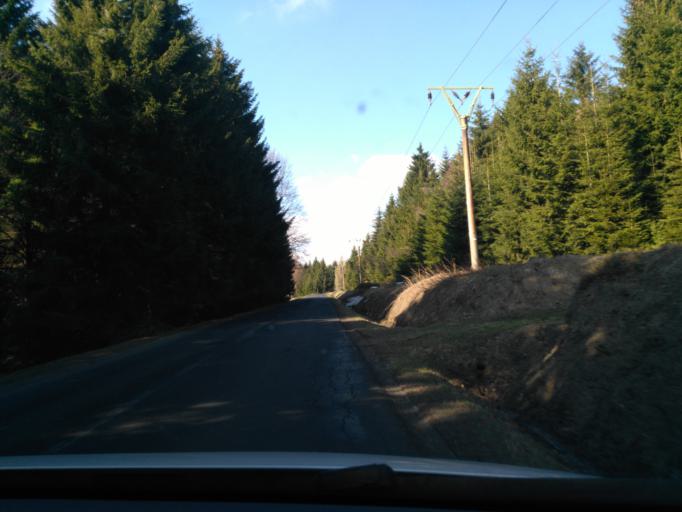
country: CZ
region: Ustecky
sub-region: Okres Chomutov
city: Kovarska
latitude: 50.4571
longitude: 13.0865
